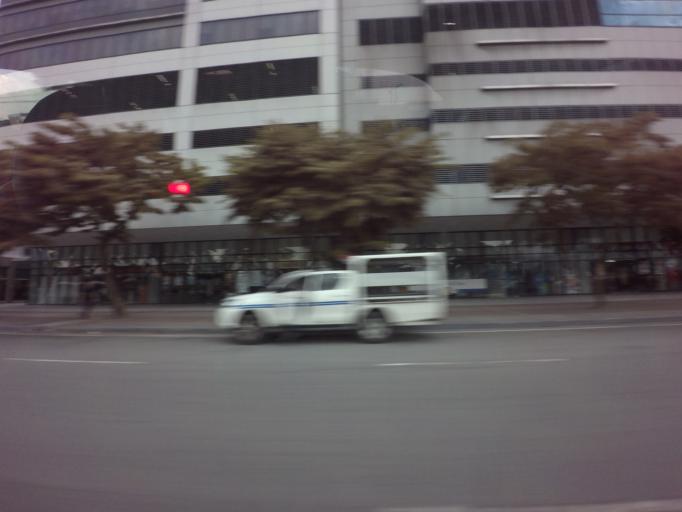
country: PH
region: Metro Manila
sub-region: Makati City
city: Makati City
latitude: 14.5294
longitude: 120.9920
